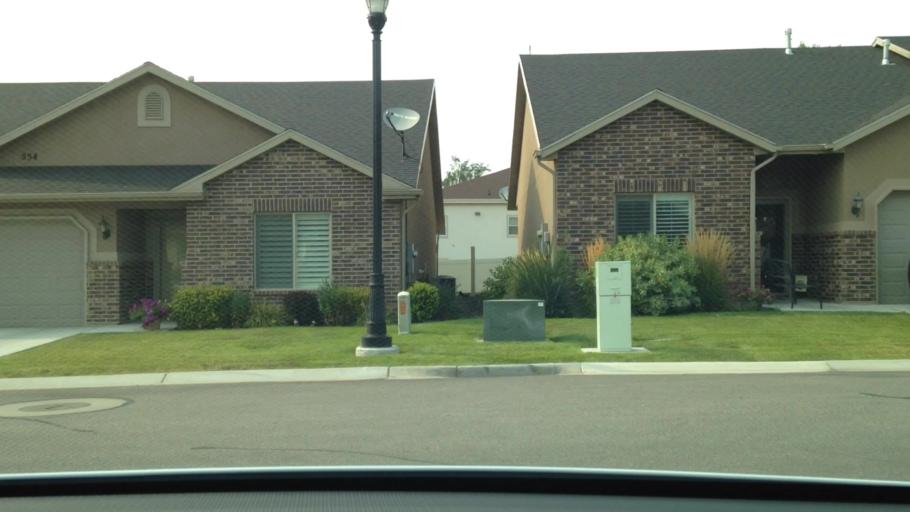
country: US
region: Utah
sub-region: Davis County
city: Kaysville
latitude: 41.0446
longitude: -111.9486
